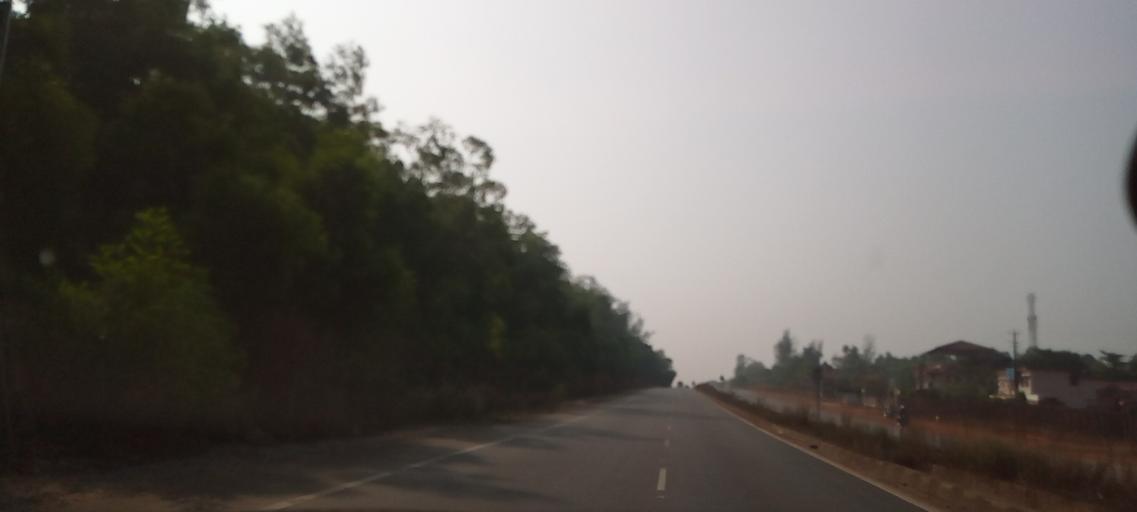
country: IN
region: Karnataka
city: Gangolli
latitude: 13.6760
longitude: 74.7000
